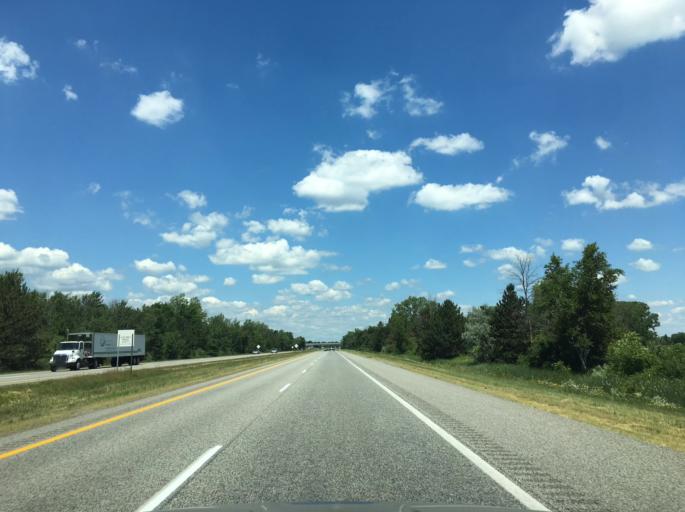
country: US
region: Michigan
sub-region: Midland County
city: Midland
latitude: 43.6336
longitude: -84.1820
